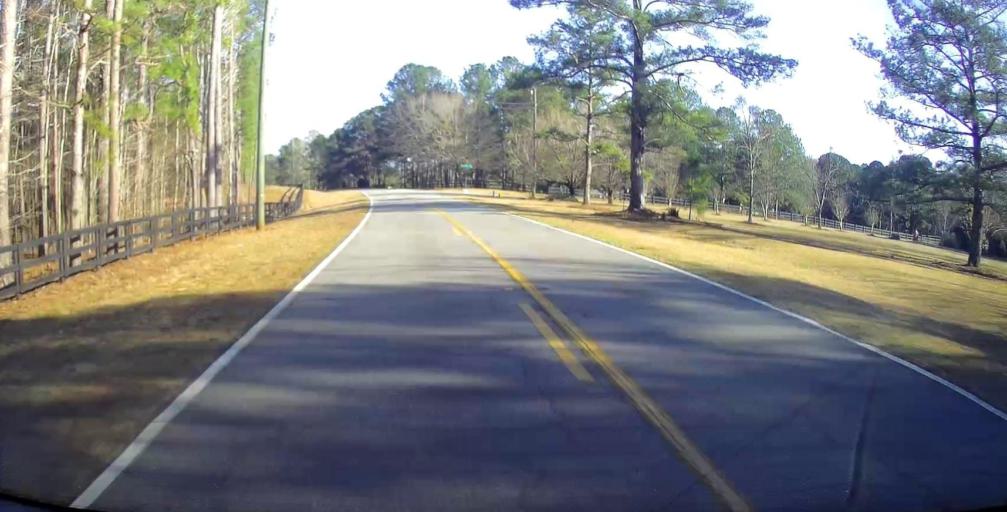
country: US
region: Georgia
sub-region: Harris County
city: Hamilton
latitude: 32.5623
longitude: -84.7913
